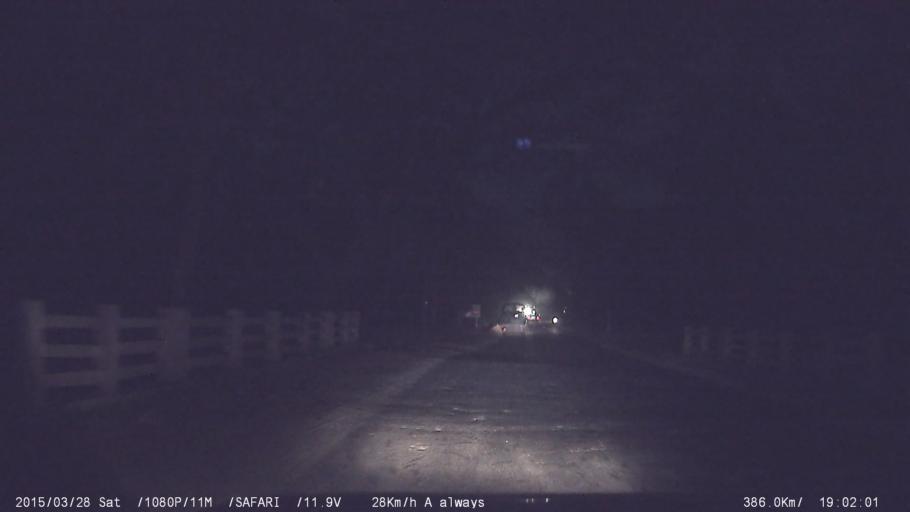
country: IN
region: Karnataka
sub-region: Mandya
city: Shrirangapattana
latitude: 12.3904
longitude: 76.5913
